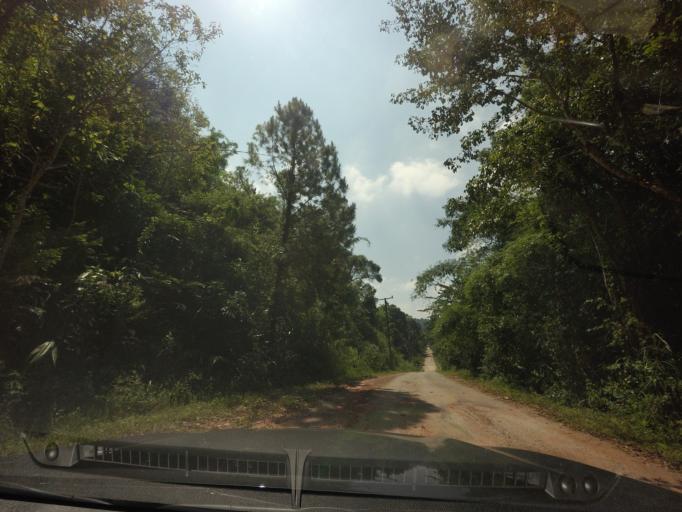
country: TH
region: Loei
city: Na Haeo
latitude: 17.5192
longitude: 100.9387
